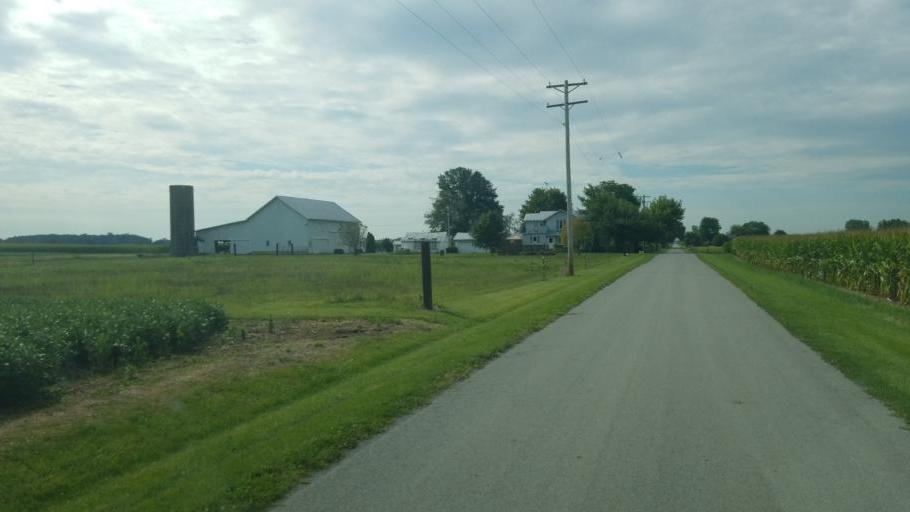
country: US
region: Ohio
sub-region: Wyandot County
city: Upper Sandusky
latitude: 40.7601
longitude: -83.1690
